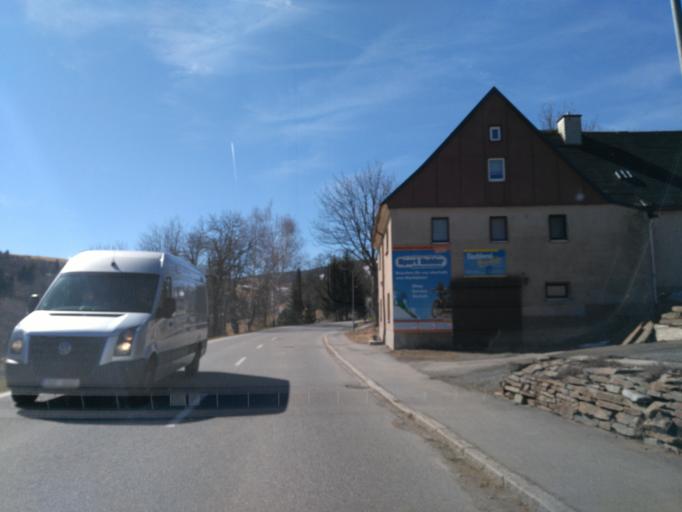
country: DE
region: Saxony
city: Kurort Oberwiesenthal
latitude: 50.4278
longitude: 12.9884
